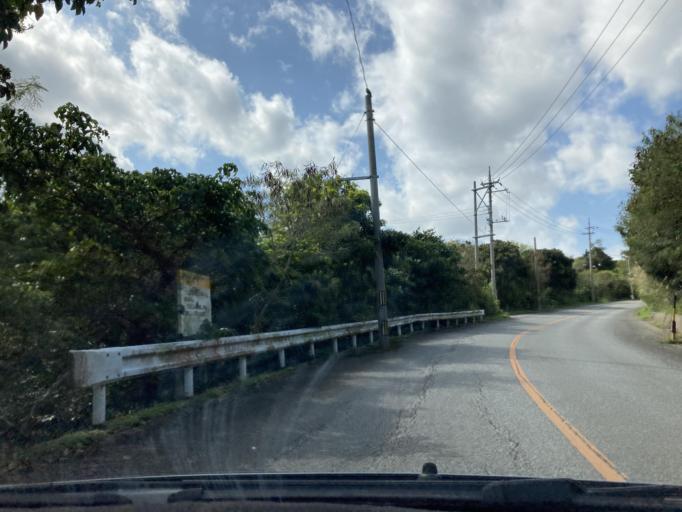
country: JP
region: Okinawa
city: Ginowan
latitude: 26.1824
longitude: 127.7646
